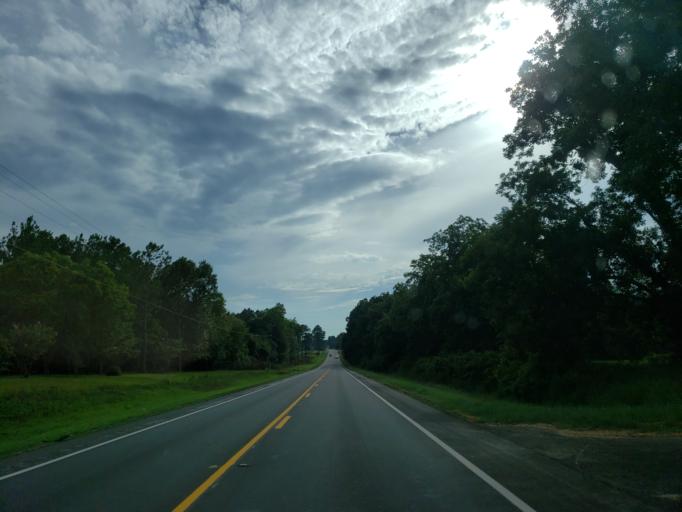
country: US
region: Georgia
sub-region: Irwin County
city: Ocilla
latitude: 31.5615
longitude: -83.3552
